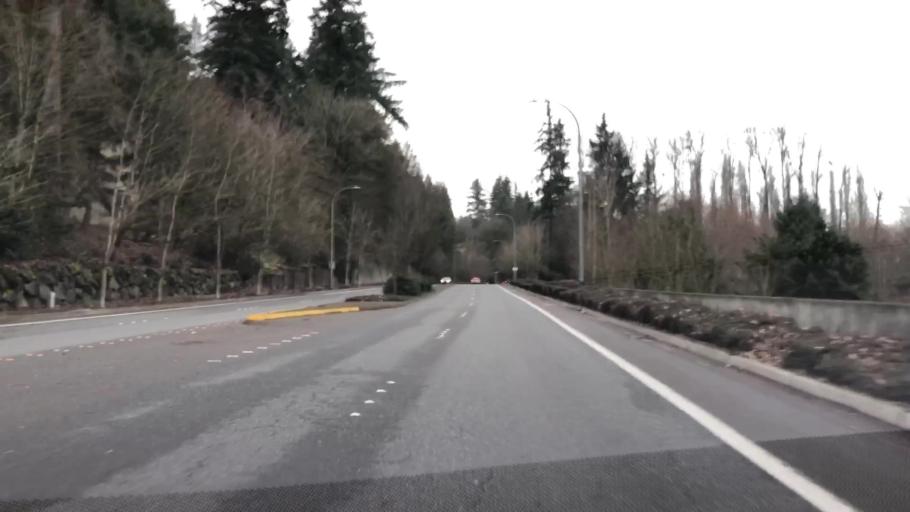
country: US
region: Washington
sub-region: King County
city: Redmond
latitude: 47.6595
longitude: -122.1233
